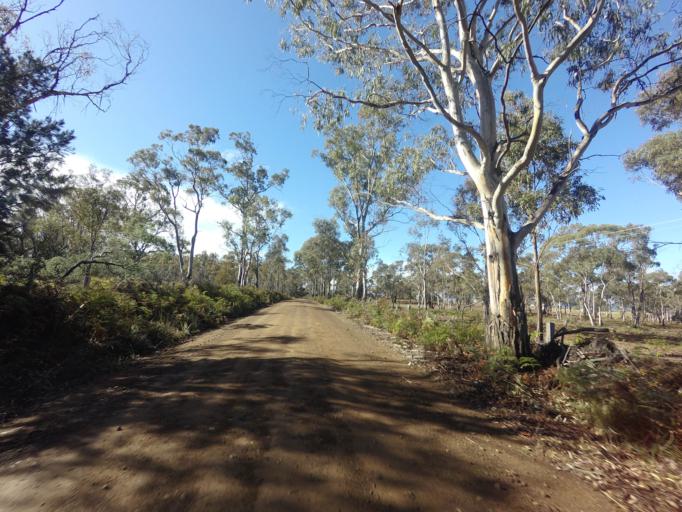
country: AU
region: Tasmania
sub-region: Sorell
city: Sorell
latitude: -42.4027
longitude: 147.9741
